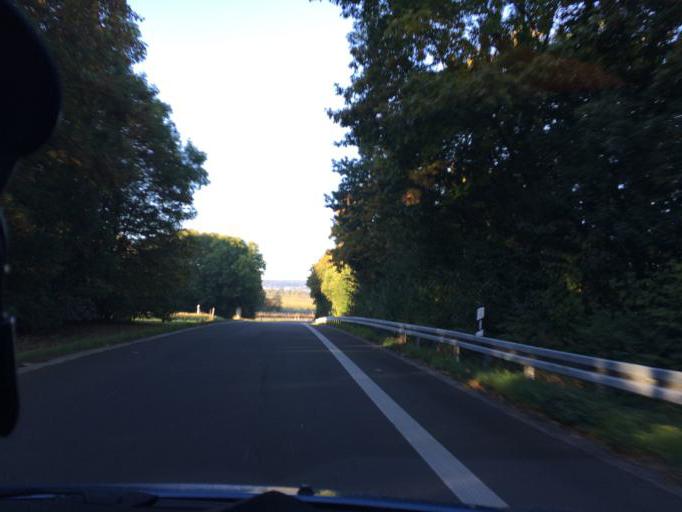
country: DE
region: North Rhine-Westphalia
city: Meckenheim
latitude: 50.5945
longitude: 7.0307
